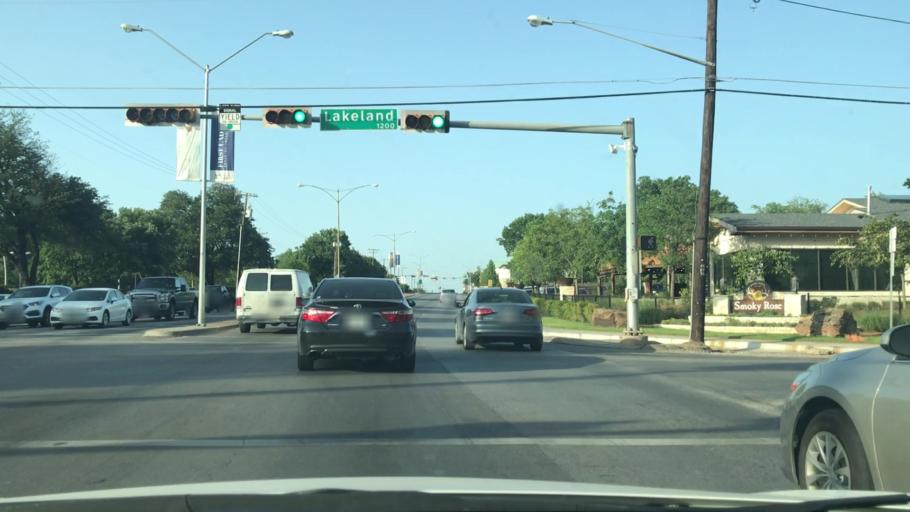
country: US
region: Texas
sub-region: Dallas County
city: Highland Park
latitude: 32.8230
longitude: -96.7149
